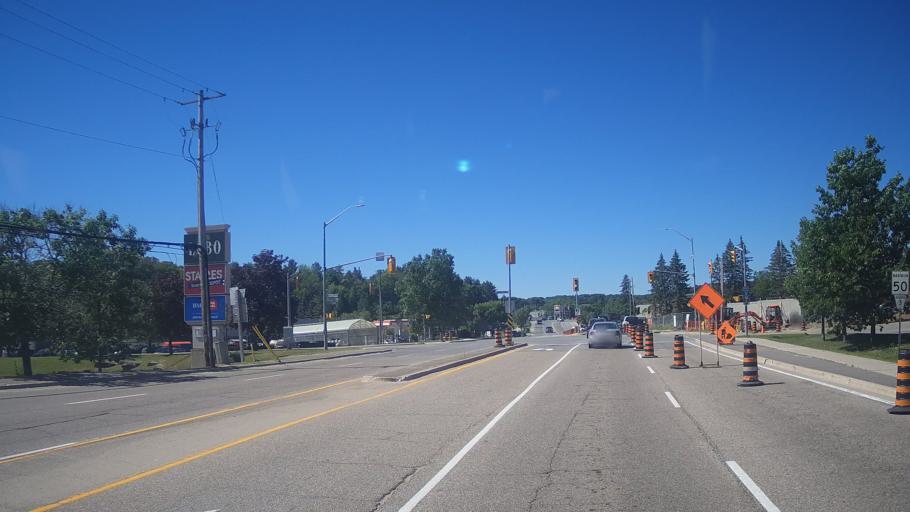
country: CA
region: Ontario
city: Huntsville
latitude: 45.3358
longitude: -79.2046
